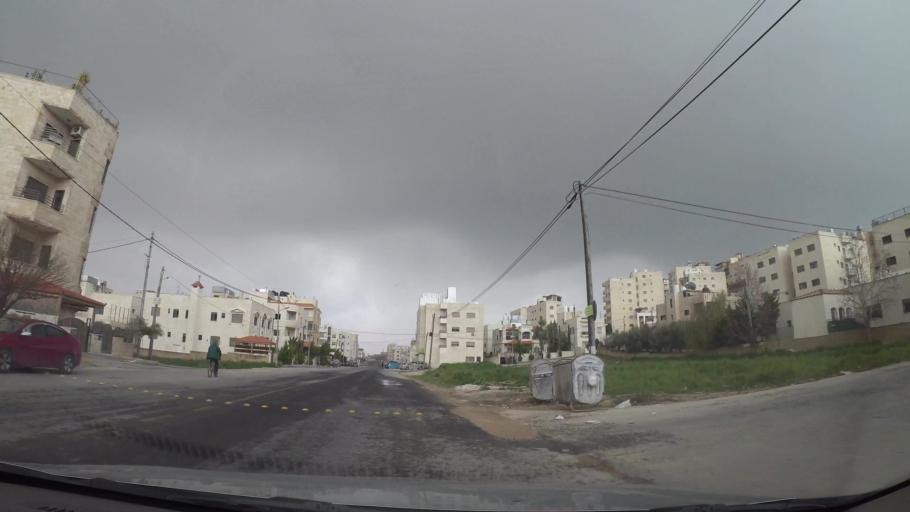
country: JO
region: Amman
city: Umm as Summaq
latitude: 31.8841
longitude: 35.8526
